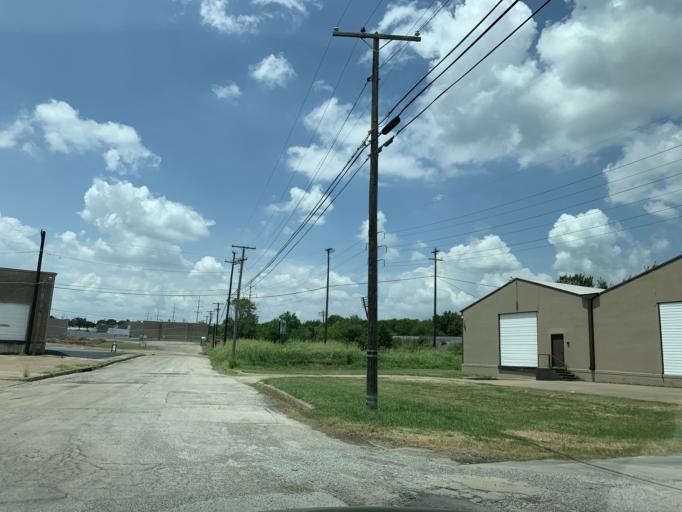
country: US
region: Texas
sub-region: Tarrant County
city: Forest Hill
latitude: 32.7313
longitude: -97.2306
